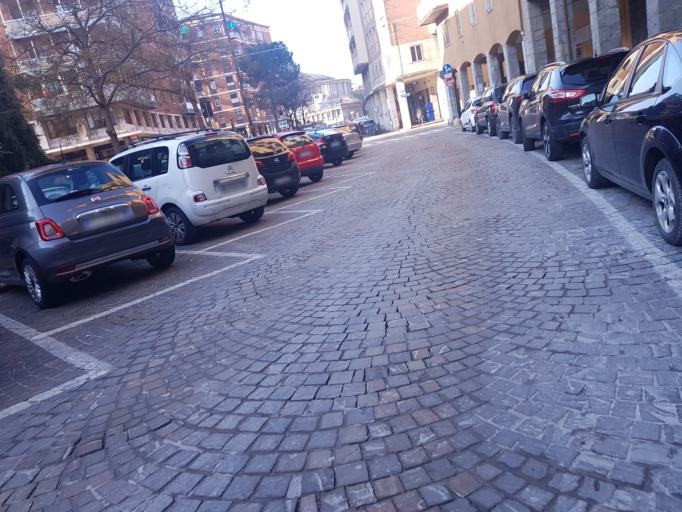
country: IT
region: Emilia-Romagna
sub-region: Provincia di Bologna
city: Bologna
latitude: 44.5004
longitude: 11.3350
